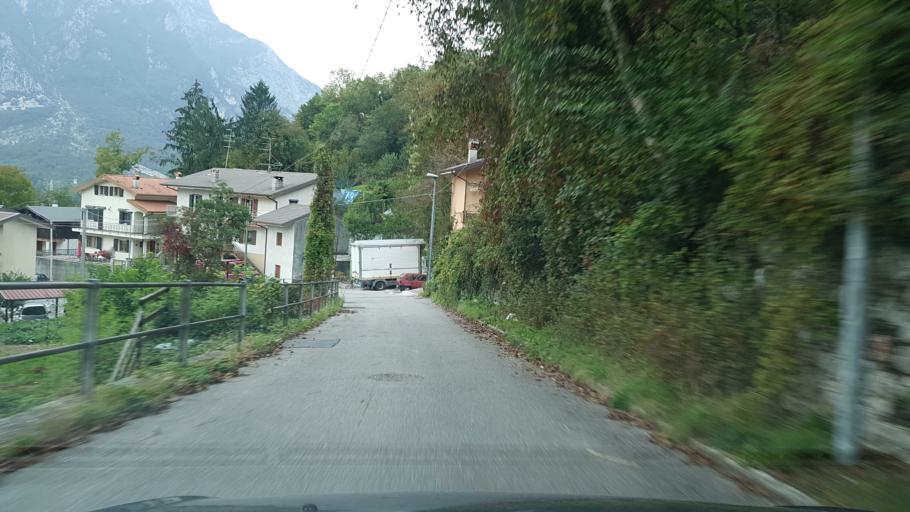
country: IT
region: Friuli Venezia Giulia
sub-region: Provincia di Udine
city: Venzone
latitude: 46.3351
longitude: 13.1472
